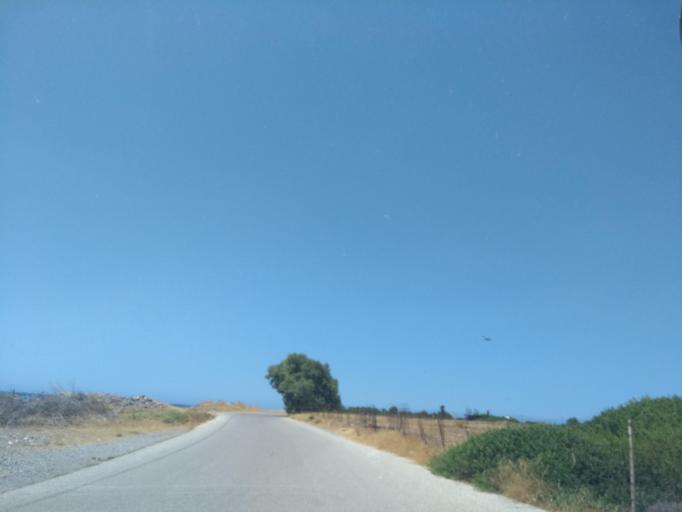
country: GR
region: Crete
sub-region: Nomos Chanias
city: Vryses
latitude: 35.3563
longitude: 23.5329
